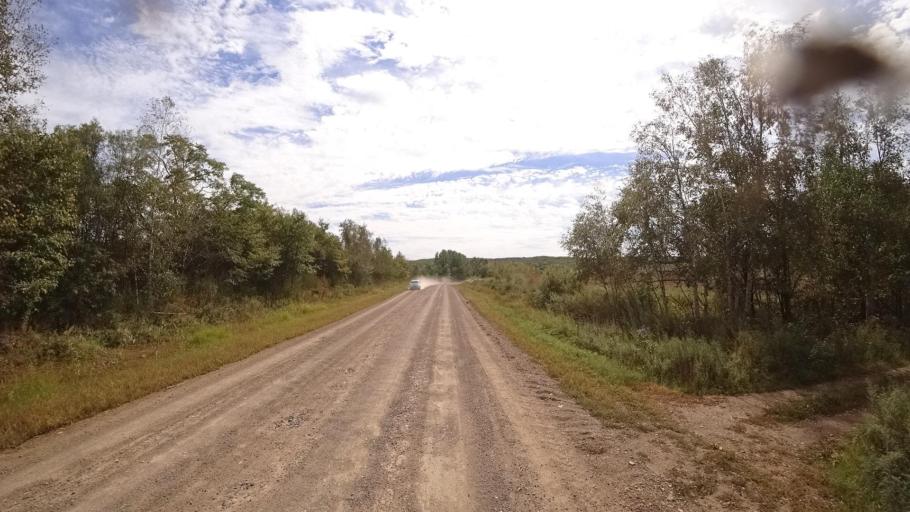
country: RU
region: Primorskiy
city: Yakovlevka
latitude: 44.5640
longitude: 133.5958
